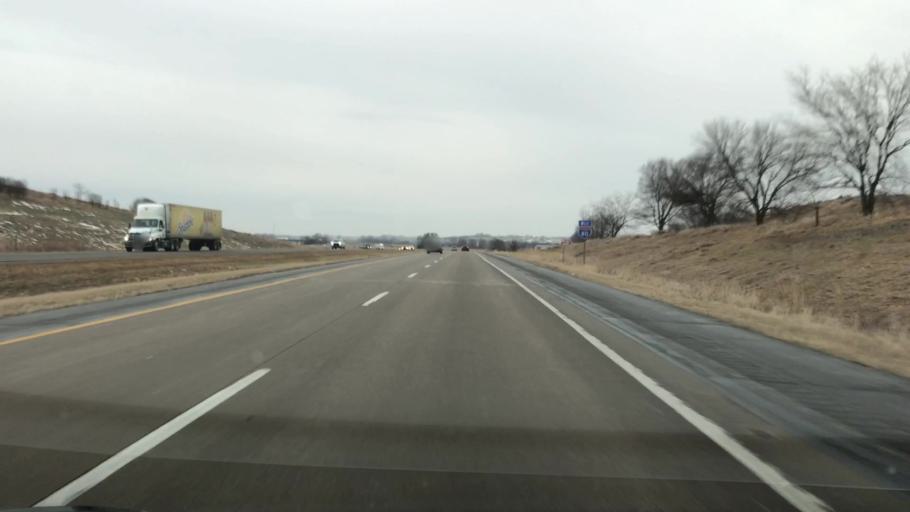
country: US
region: Iowa
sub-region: Pottawattamie County
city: Oakland
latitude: 41.4376
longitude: -95.6192
